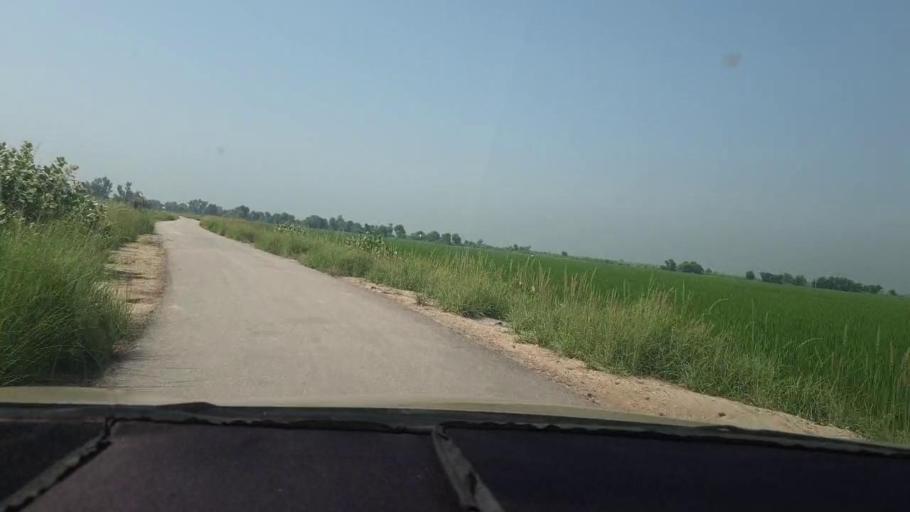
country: PK
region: Sindh
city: Kambar
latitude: 27.5598
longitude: 68.0429
